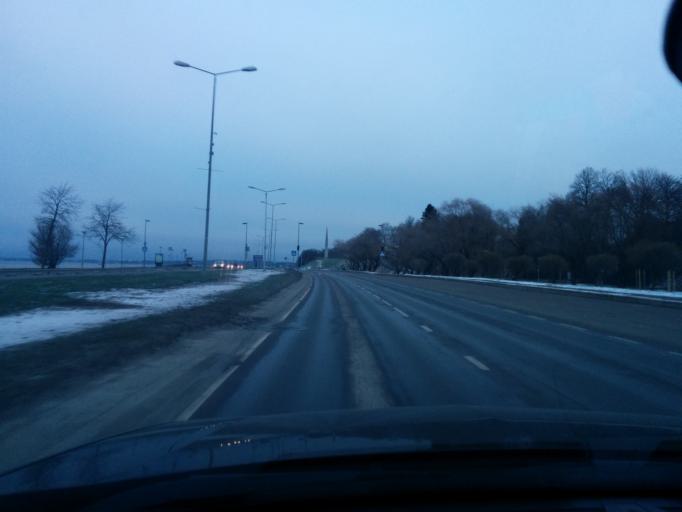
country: EE
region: Harju
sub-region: Tallinna linn
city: Tallinn
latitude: 59.4506
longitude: 24.8064
